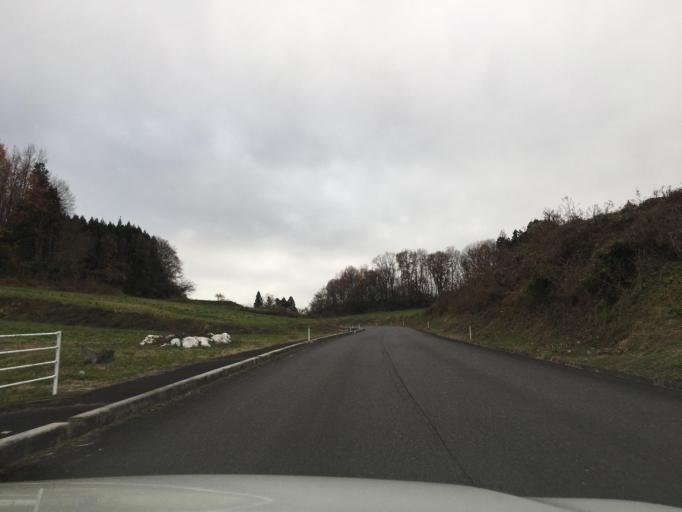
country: JP
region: Fukushima
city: Funehikimachi-funehiki
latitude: 37.4677
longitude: 140.5450
